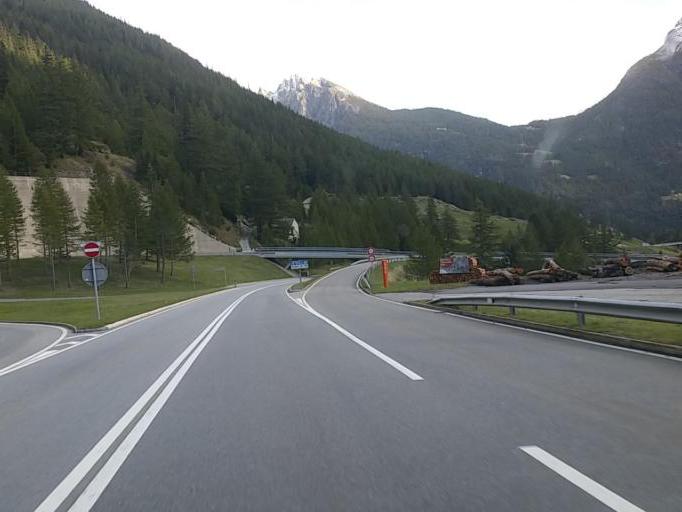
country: CH
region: Valais
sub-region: Brig District
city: Brig
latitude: 46.2005
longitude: 8.0552
